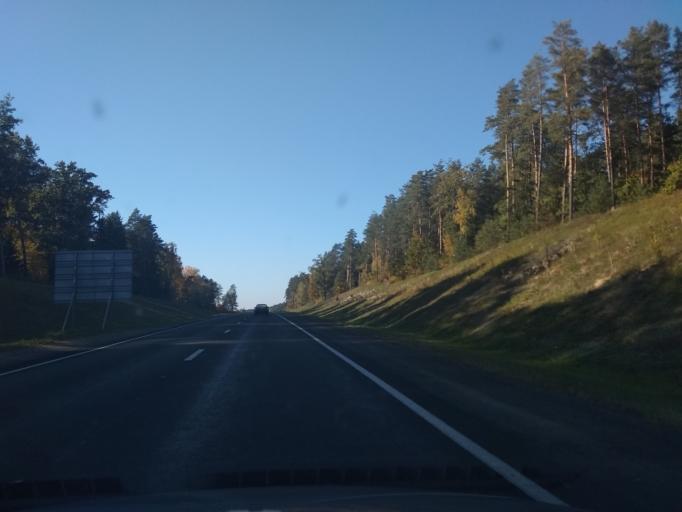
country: BY
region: Grodnenskaya
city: Zhyrovichy
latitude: 53.0479
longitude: 25.3500
